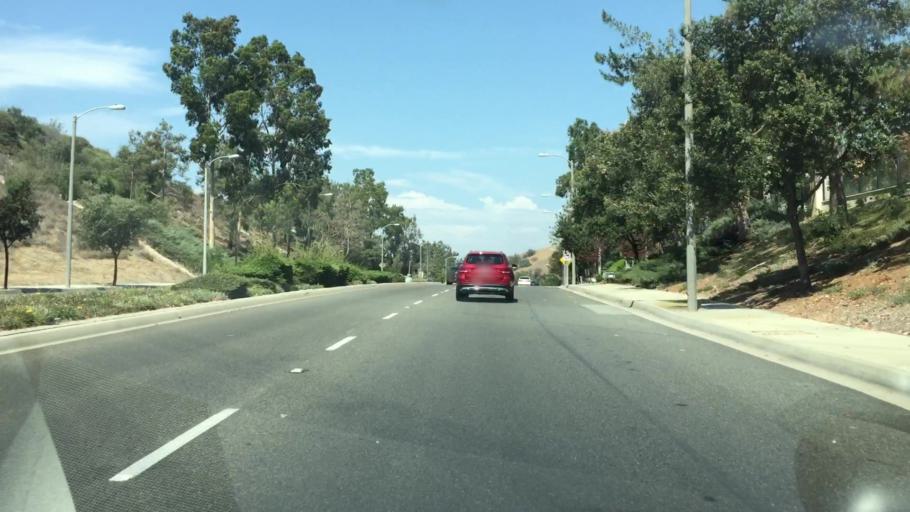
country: US
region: California
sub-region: Los Angeles County
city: Rowland Heights
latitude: 33.9586
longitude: -117.9198
